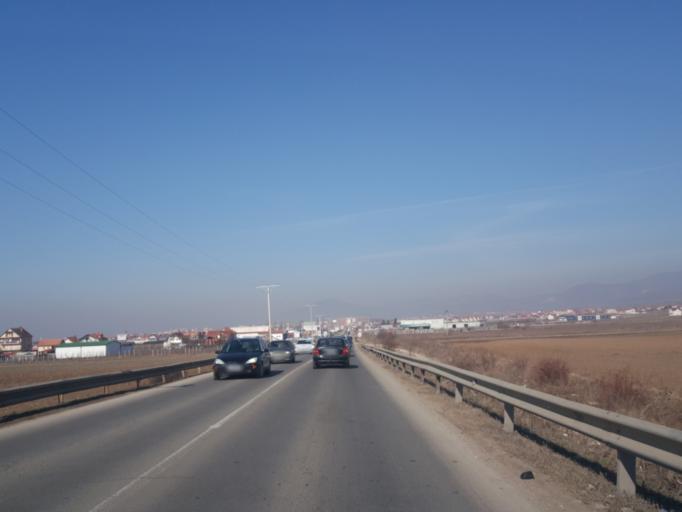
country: XK
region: Mitrovica
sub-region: Vushtrri
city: Vushtrri
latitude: 42.8029
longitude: 20.9932
